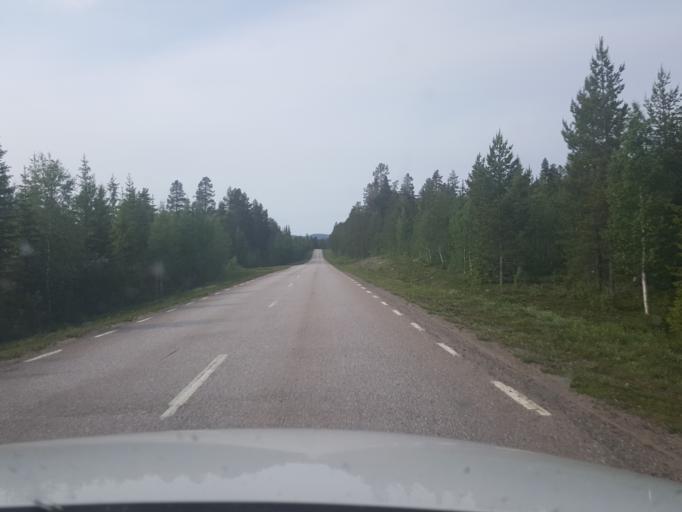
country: SE
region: Norrbotten
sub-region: Arjeplogs Kommun
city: Arjeplog
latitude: 65.7729
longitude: 18.0158
